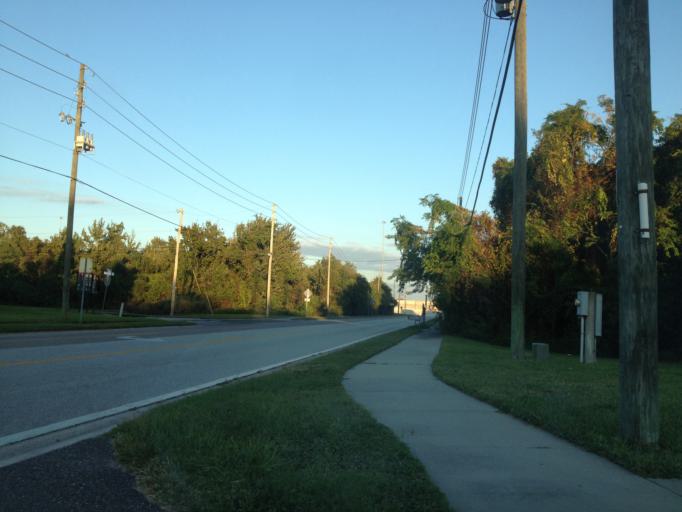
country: US
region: Florida
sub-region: Pinellas County
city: South Highpoint
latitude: 27.9568
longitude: -82.7334
